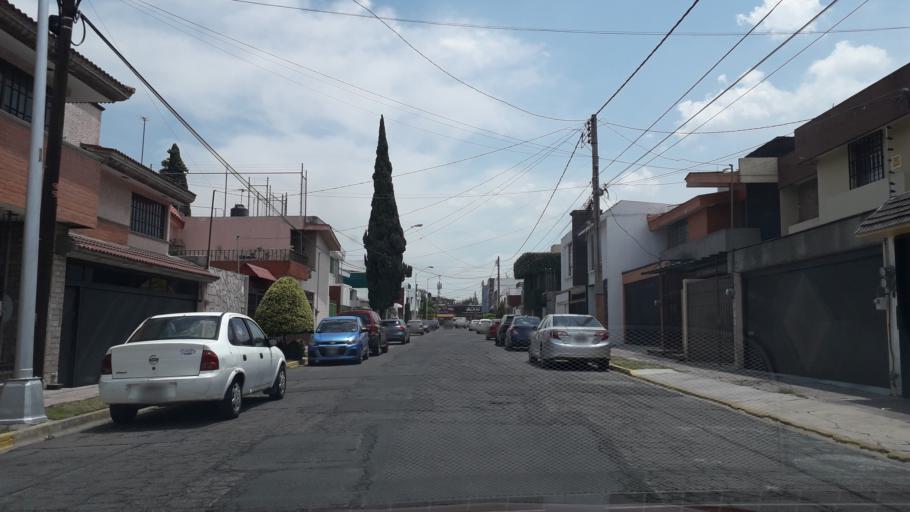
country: MX
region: Puebla
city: Puebla
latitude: 19.0196
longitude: -98.1937
